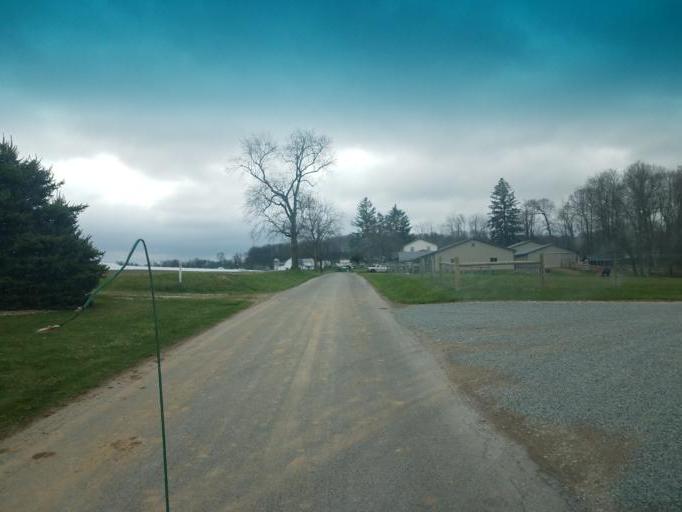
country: US
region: Ohio
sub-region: Stark County
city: Beach City
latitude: 40.6296
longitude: -81.6777
